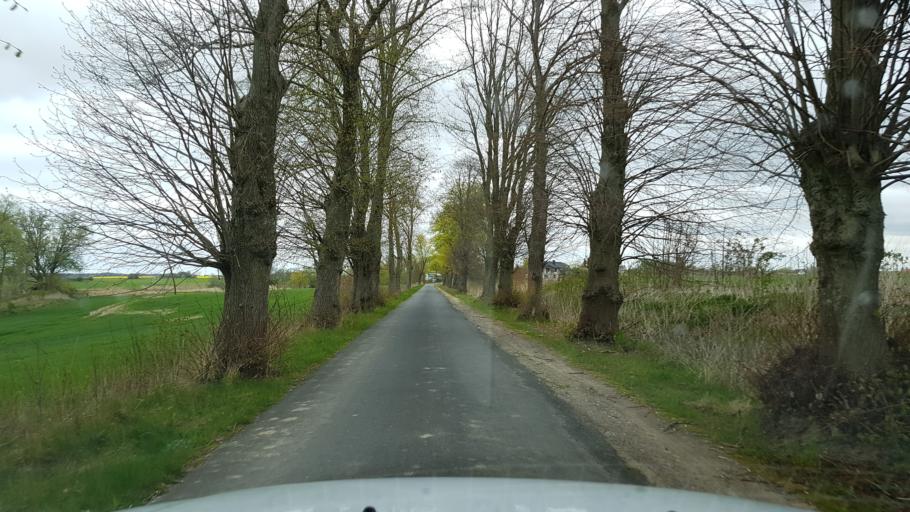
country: PL
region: West Pomeranian Voivodeship
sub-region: Powiat koszalinski
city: Mielno
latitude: 54.2288
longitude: 16.0411
